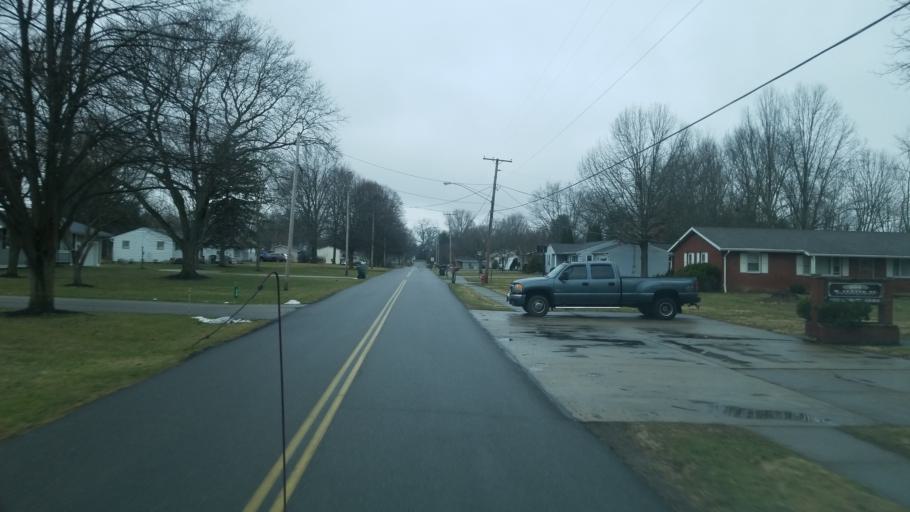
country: US
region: Ohio
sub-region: Wayne County
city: Smithville
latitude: 40.8587
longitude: -81.8563
